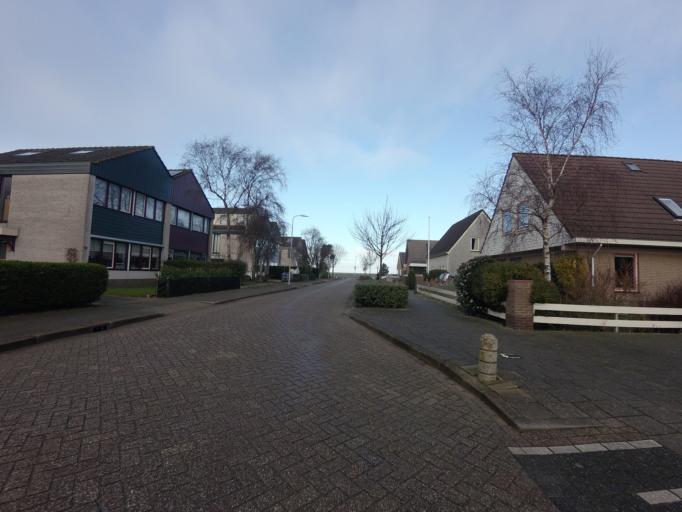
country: NL
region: North Holland
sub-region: Gemeente Texel
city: Den Burg
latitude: 53.1569
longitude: 4.8680
